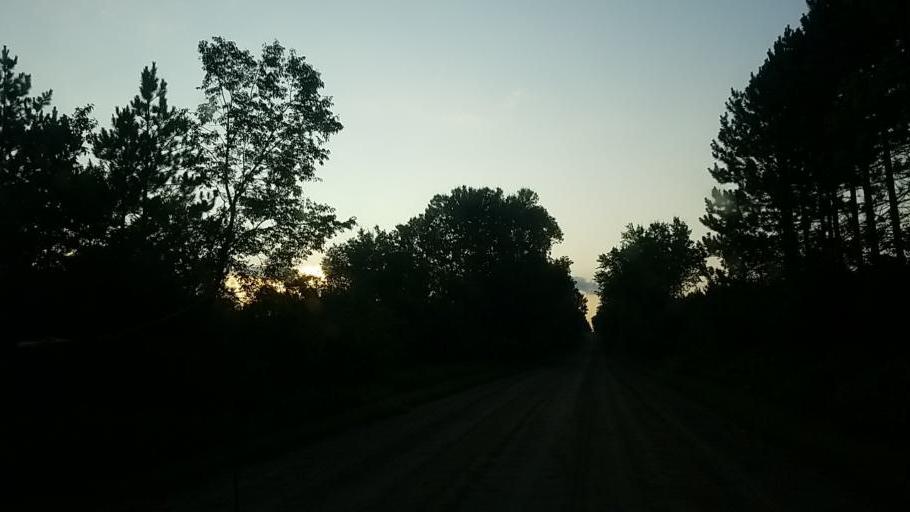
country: US
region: Michigan
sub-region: Osceola County
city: Evart
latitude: 43.9151
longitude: -85.1737
